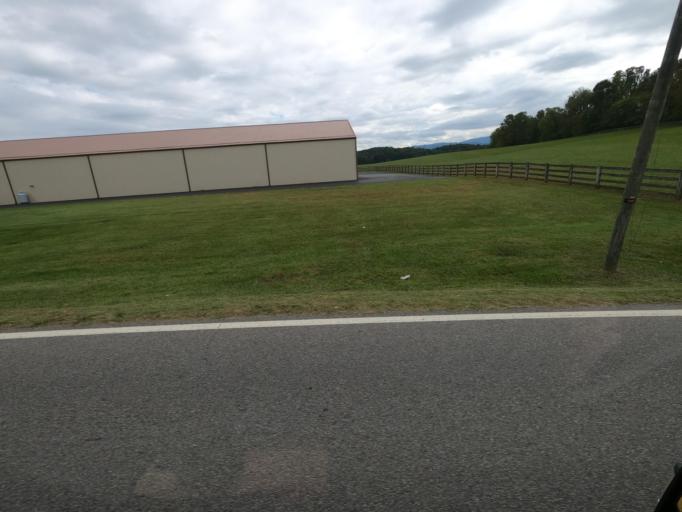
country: US
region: Tennessee
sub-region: Washington County
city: Jonesborough
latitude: 36.2317
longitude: -82.5597
